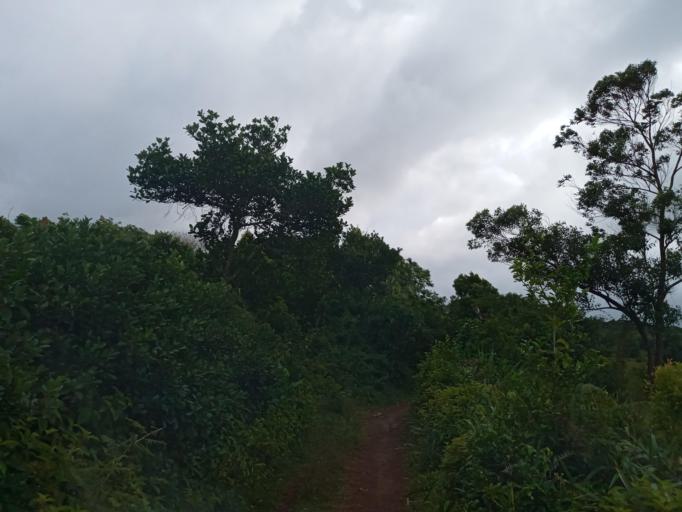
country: MG
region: Atsimo-Atsinanana
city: Vohipaho
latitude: -23.7758
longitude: 47.5359
